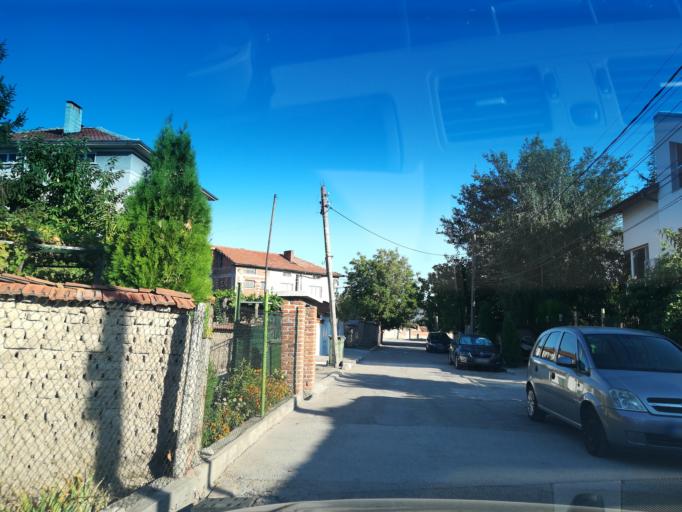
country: BG
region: Stara Zagora
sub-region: Obshtina Chirpan
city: Chirpan
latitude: 42.1065
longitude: 25.2188
